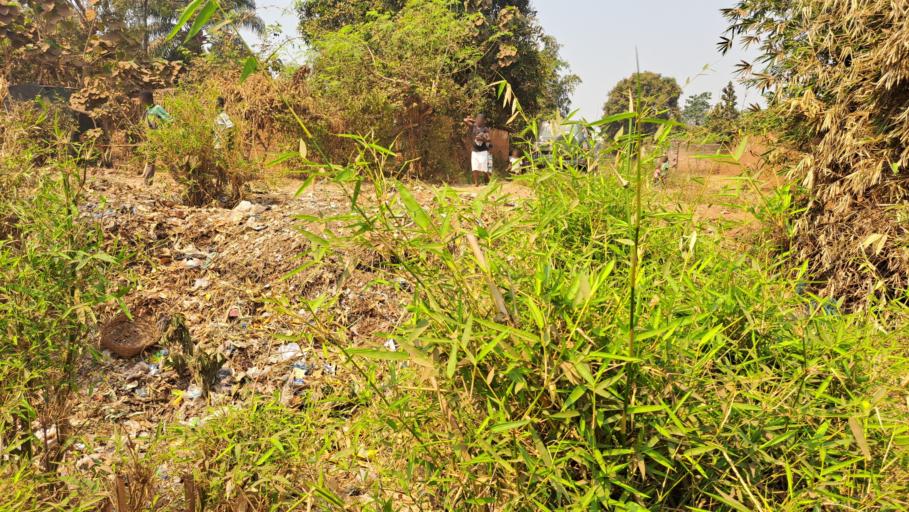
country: CD
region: Kasai-Oriental
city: Mbuji-Mayi
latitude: -6.1241
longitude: 23.6099
